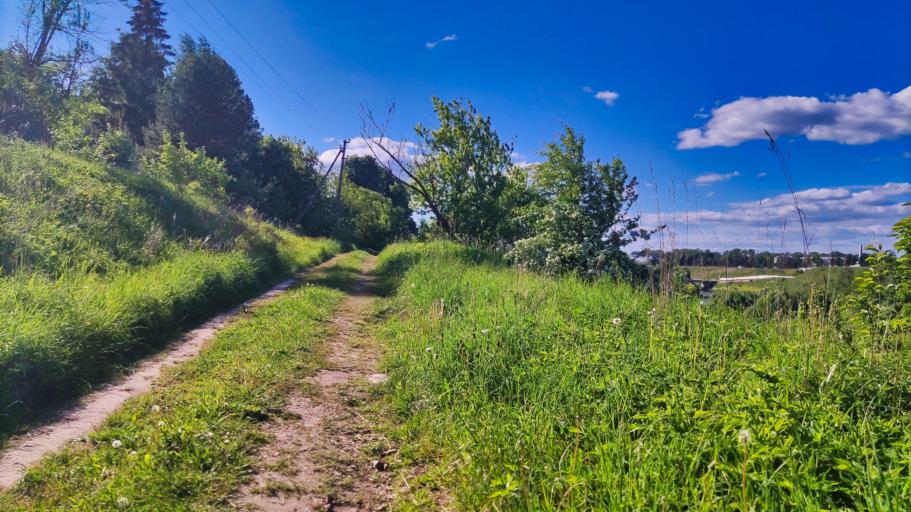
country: RU
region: Tverskaya
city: Rzhev
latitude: 56.2528
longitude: 34.3424
